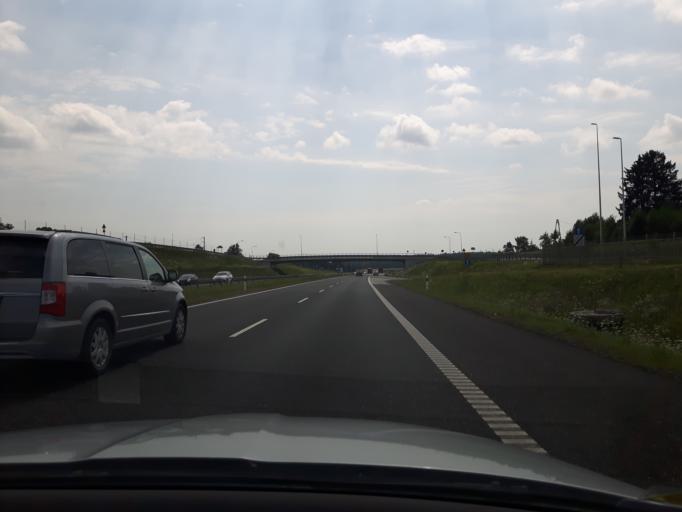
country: PL
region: Warmian-Masurian Voivodeship
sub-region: Powiat olsztynski
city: Olsztynek
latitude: 53.4795
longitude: 20.3211
